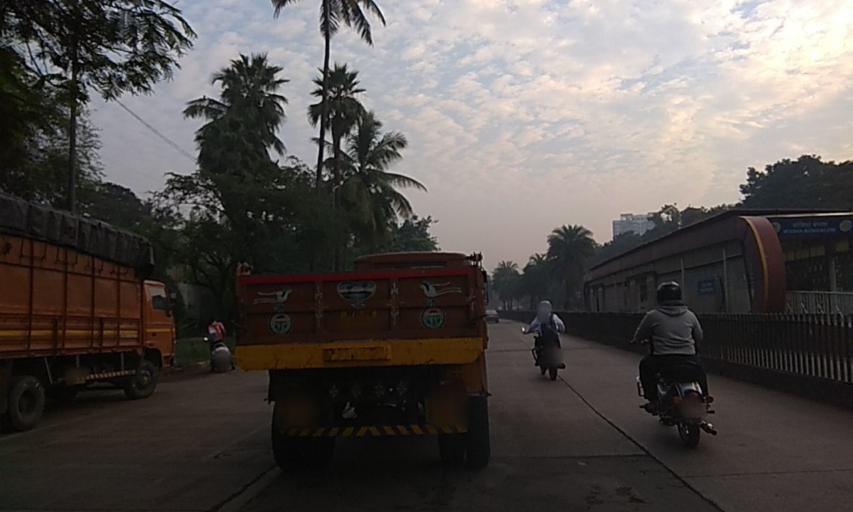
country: IN
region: Maharashtra
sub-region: Pune Division
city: Khadki
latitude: 18.5482
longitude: 73.8920
